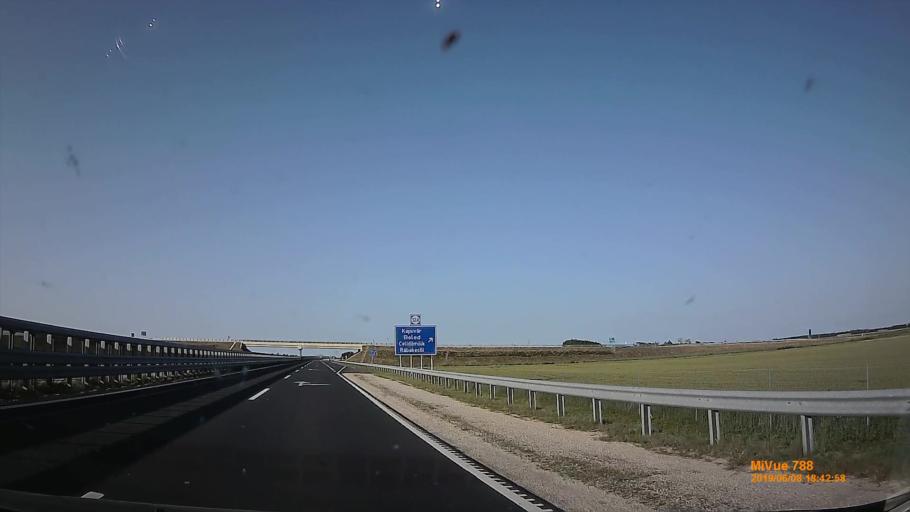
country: HU
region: Gyor-Moson-Sopron
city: Beled
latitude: 47.4491
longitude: 17.0991
